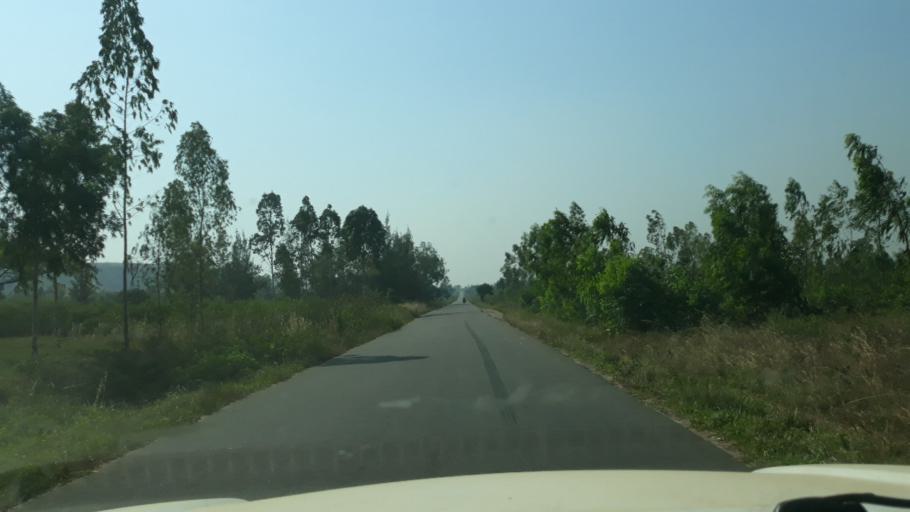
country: CD
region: South Kivu
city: Uvira
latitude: -3.2215
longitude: 29.1653
